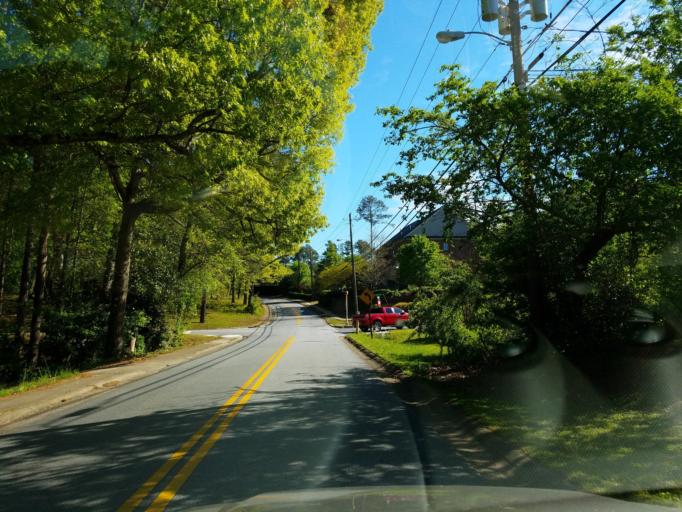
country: US
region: Georgia
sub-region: Cobb County
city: Smyrna
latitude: 33.8673
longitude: -84.5378
